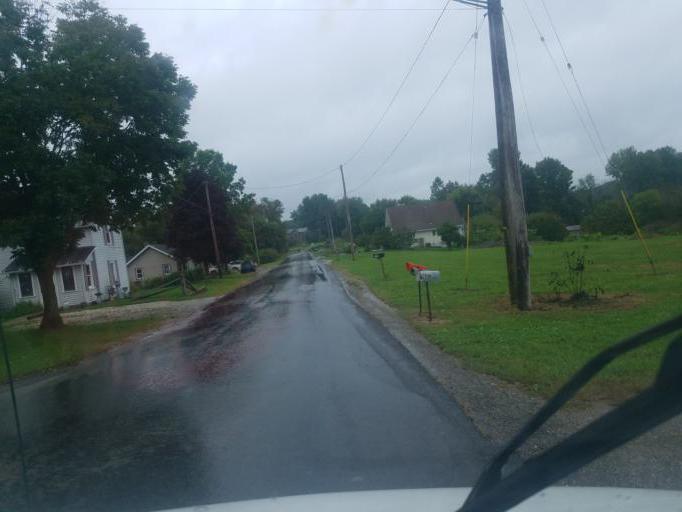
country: US
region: Ohio
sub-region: Wayne County
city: Creston
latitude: 40.9848
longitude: -81.9032
